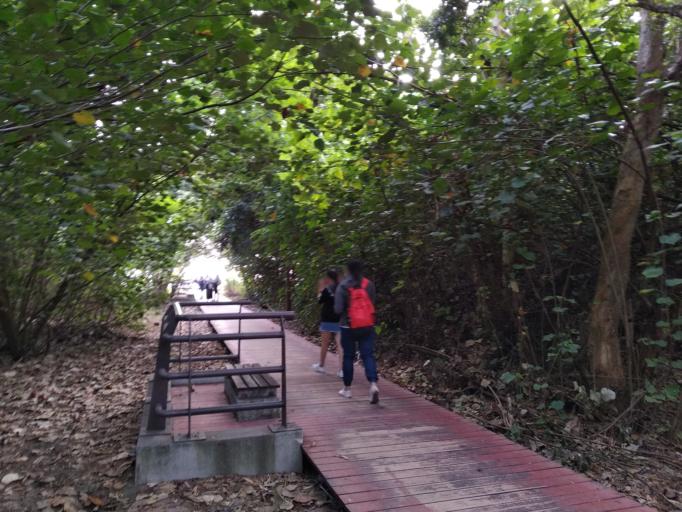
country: TW
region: Taiwan
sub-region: Tainan
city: Tainan
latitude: 22.9810
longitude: 120.1556
